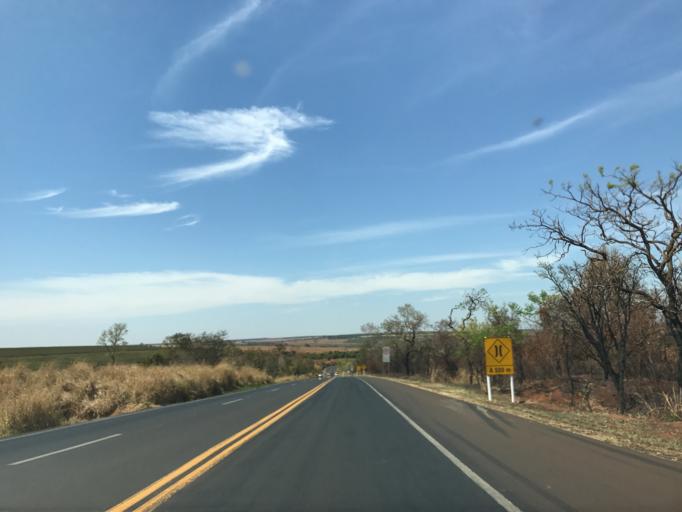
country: BR
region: Minas Gerais
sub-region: Monte Alegre De Minas
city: Monte Alegre de Minas
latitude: -19.0215
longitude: -49.0135
